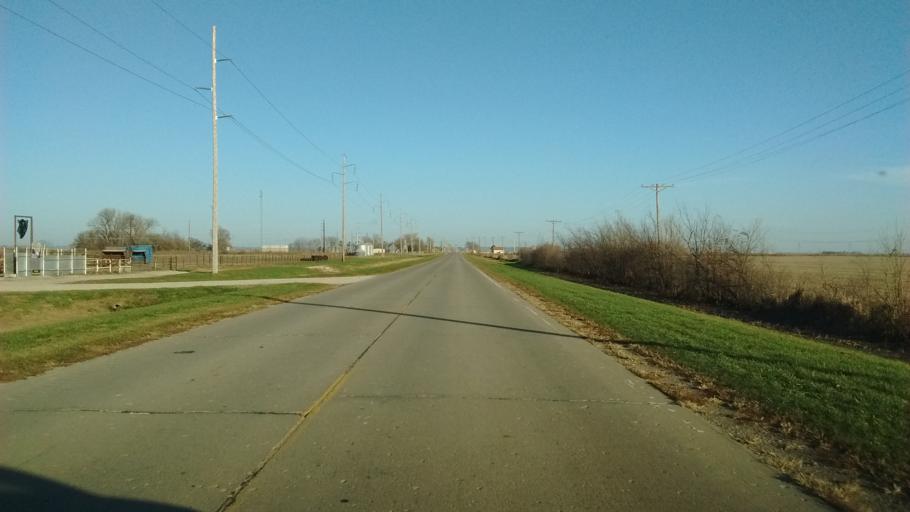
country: US
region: Iowa
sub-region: Woodbury County
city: Sergeant Bluff
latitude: 42.3302
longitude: -96.3091
